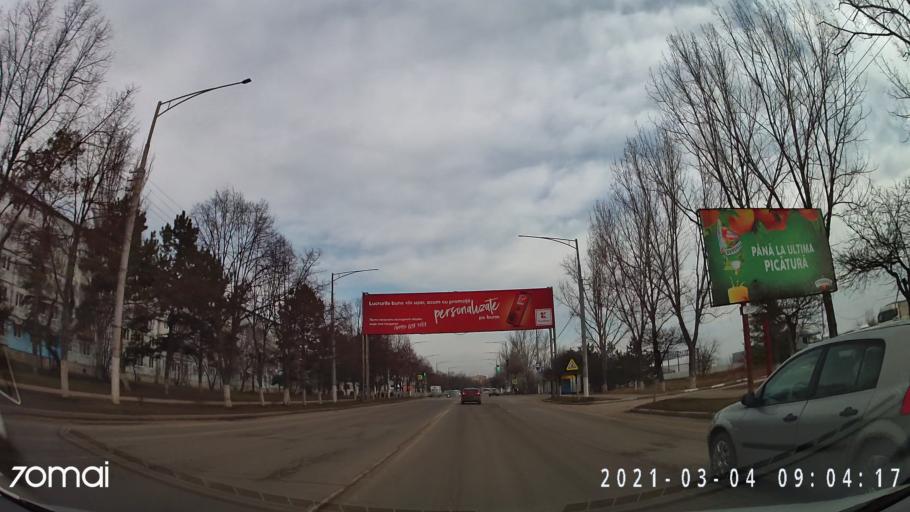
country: MD
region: Balti
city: Balti
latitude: 47.7569
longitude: 27.9412
